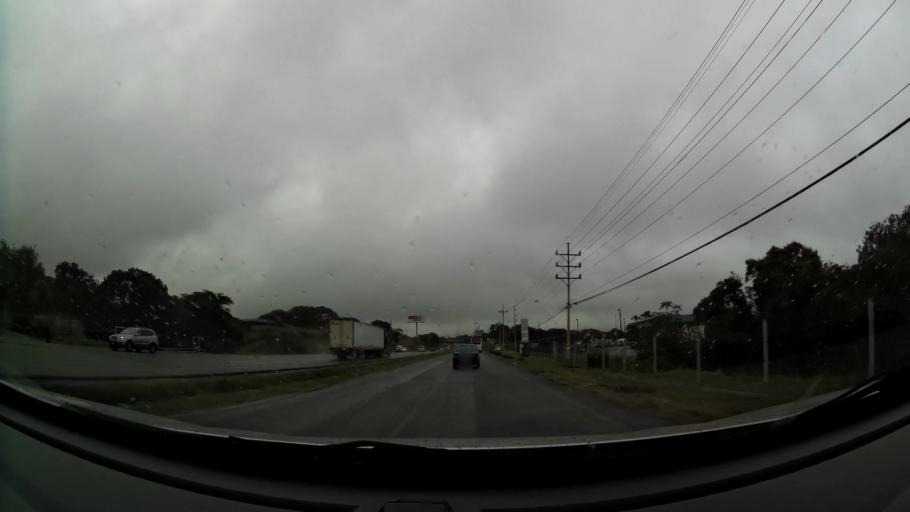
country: CR
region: Alajuela
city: Carrillos
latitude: 9.9942
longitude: -84.2523
